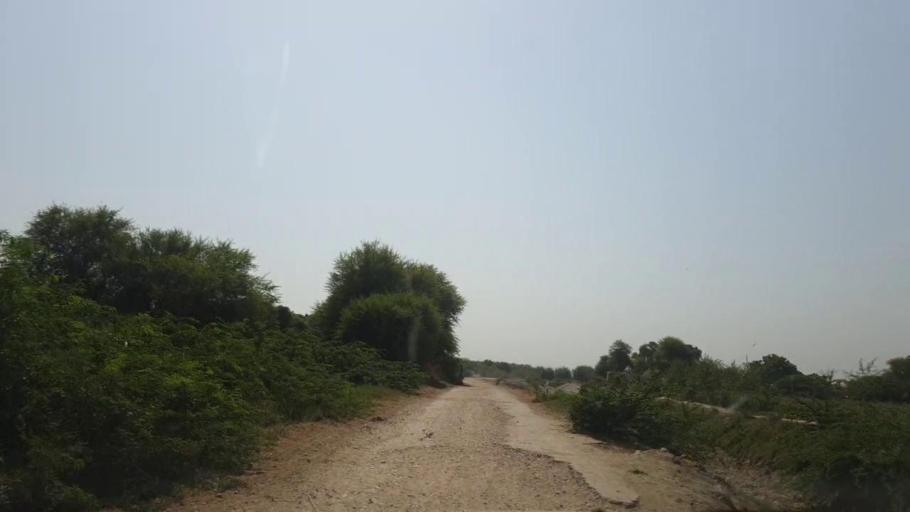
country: PK
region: Sindh
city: Jhol
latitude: 25.8689
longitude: 69.0358
